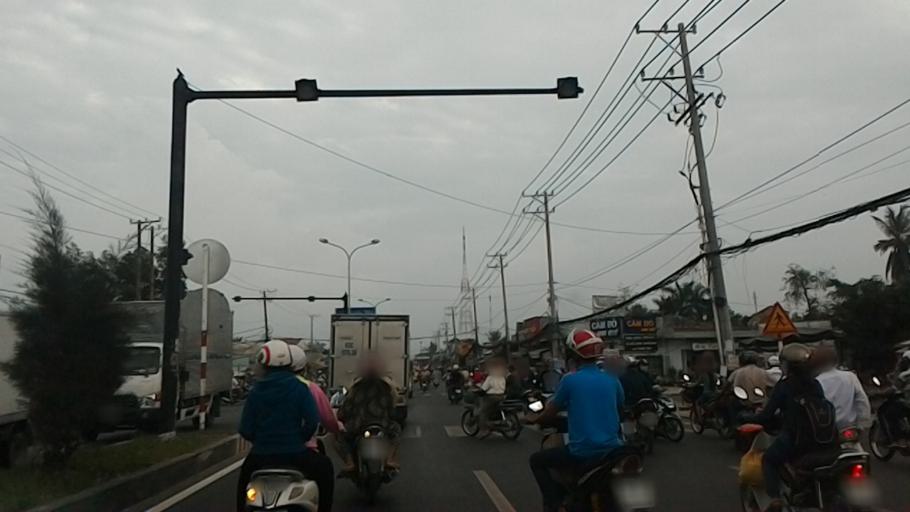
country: VN
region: Can Tho
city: Cai Rang
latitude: 10.0235
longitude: 105.7618
